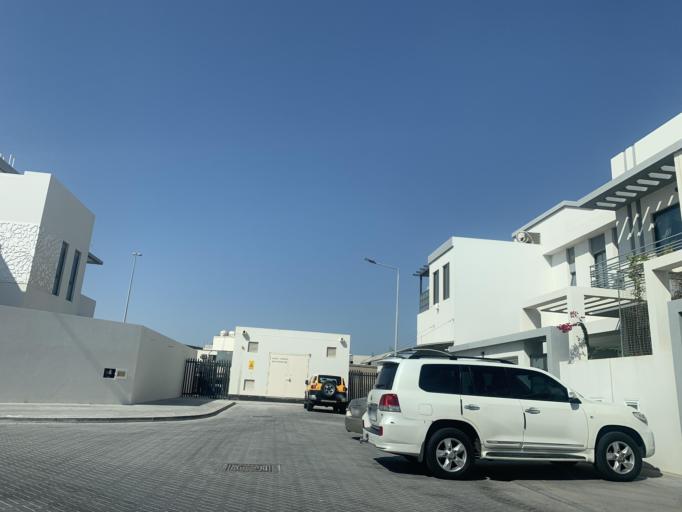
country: BH
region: Central Governorate
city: Madinat Hamad
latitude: 26.1343
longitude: 50.4831
